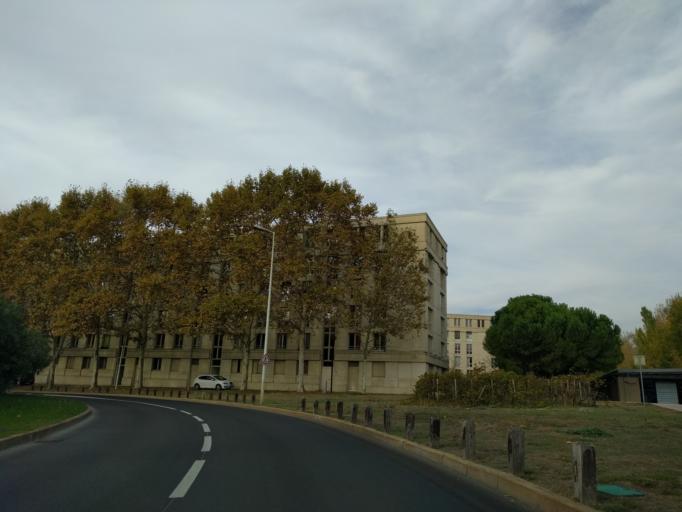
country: FR
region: Languedoc-Roussillon
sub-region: Departement de l'Herault
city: Montpellier
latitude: 43.6095
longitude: 3.8967
